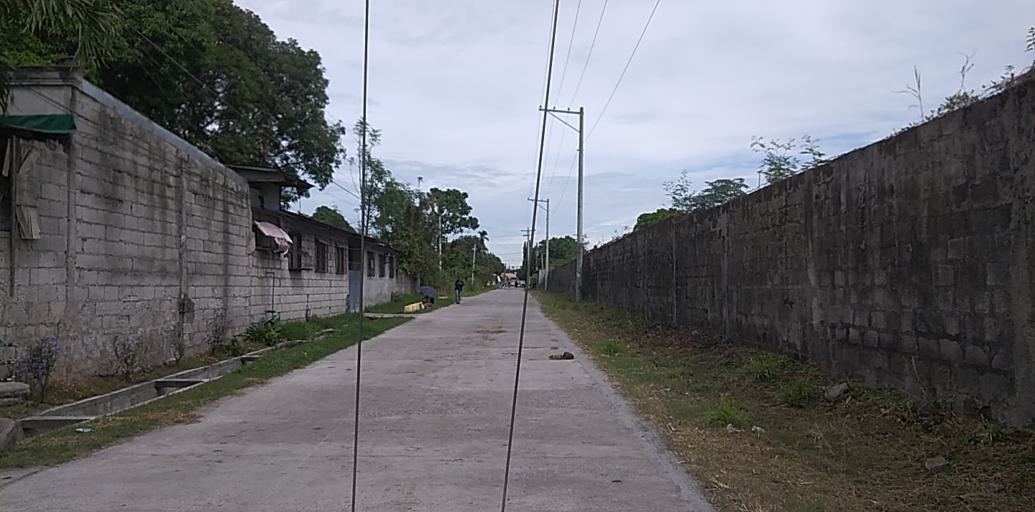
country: PH
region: Central Luzon
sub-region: Province of Pampanga
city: Manibaug Pasig
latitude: 15.1101
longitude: 120.5597
